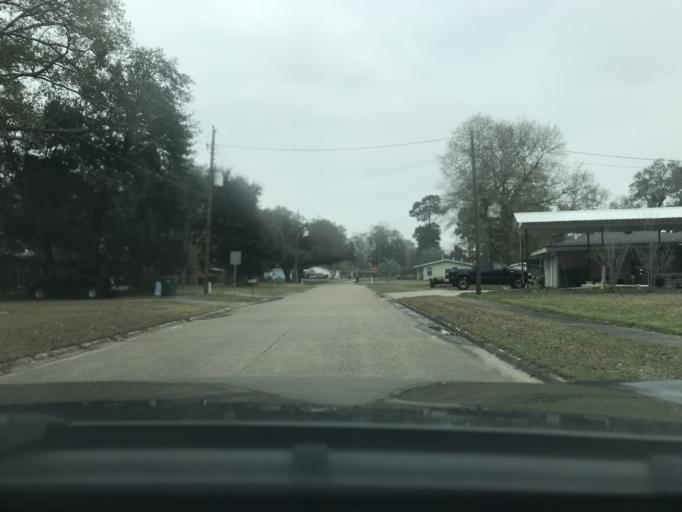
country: US
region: Louisiana
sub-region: Calcasieu Parish
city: Westlake
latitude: 30.2524
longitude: -93.2554
